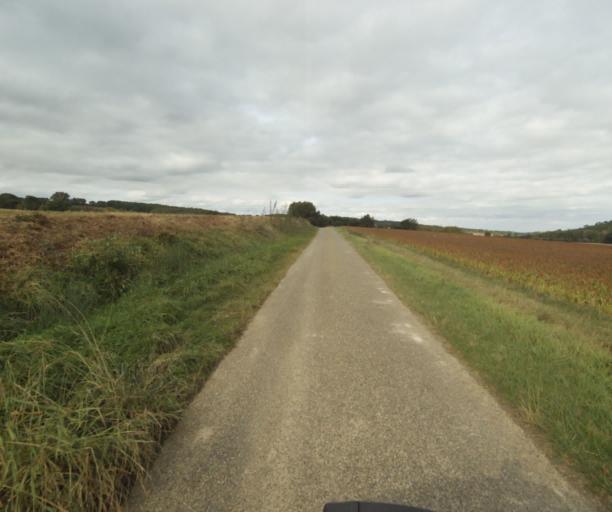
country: FR
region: Midi-Pyrenees
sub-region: Departement du Tarn-et-Garonne
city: Beaumont-de-Lomagne
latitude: 43.8205
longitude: 1.0838
